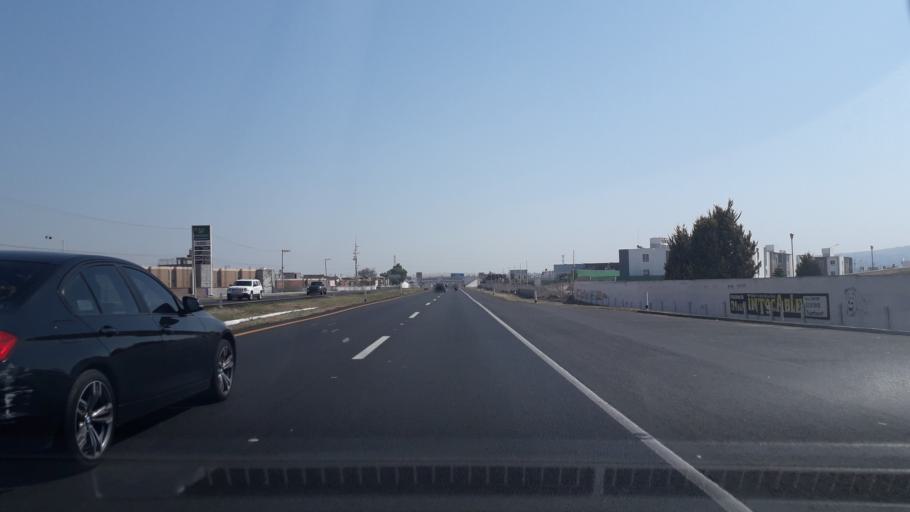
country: MX
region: Mexico
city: Santo Tomas Chiconautla
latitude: 19.6246
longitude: -99.0264
